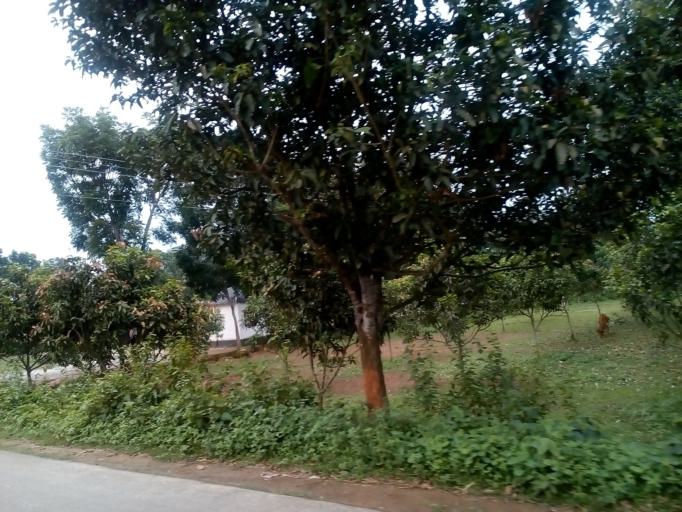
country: BD
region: Rangpur Division
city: Badarganj
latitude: 25.6100
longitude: 89.0594
